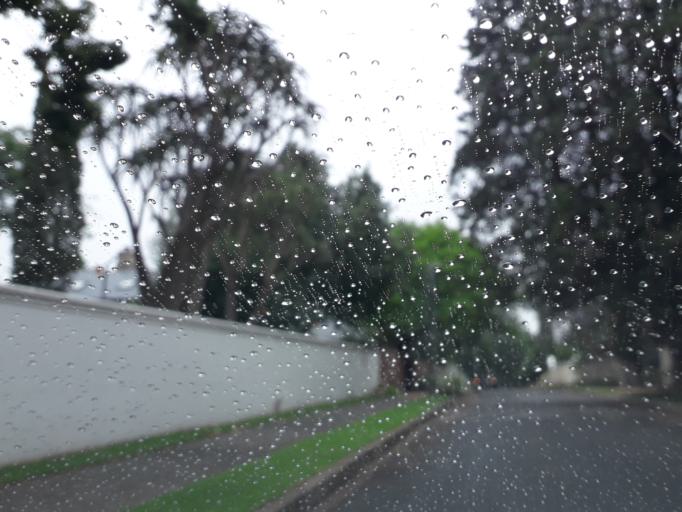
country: ZA
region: Gauteng
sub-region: City of Johannesburg Metropolitan Municipality
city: Johannesburg
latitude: -26.1381
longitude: 28.0381
